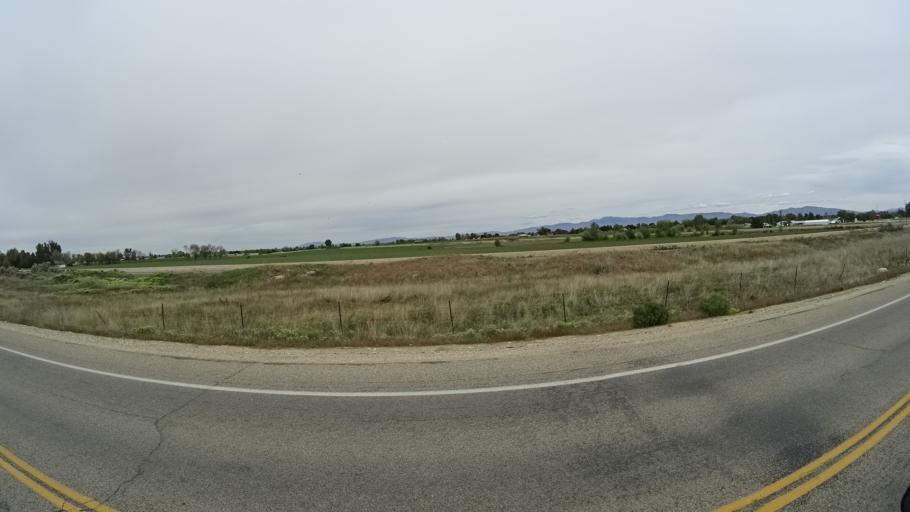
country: US
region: Idaho
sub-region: Ada County
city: Kuna
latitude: 43.4879
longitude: -116.3483
